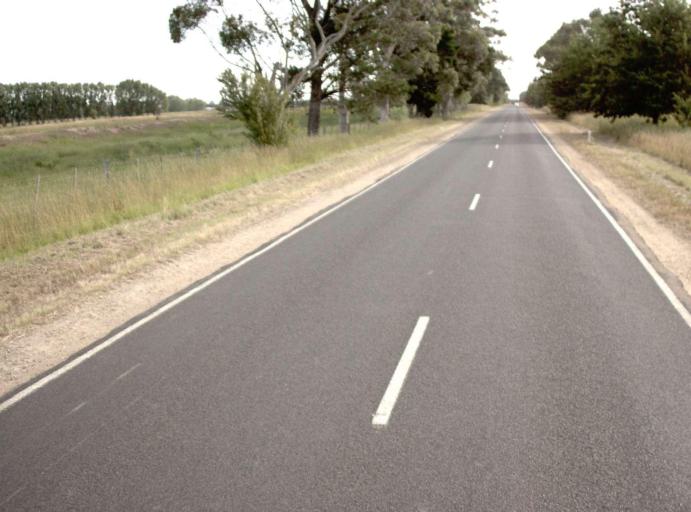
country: AU
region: Victoria
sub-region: Wellington
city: Heyfield
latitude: -38.0138
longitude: 146.7742
